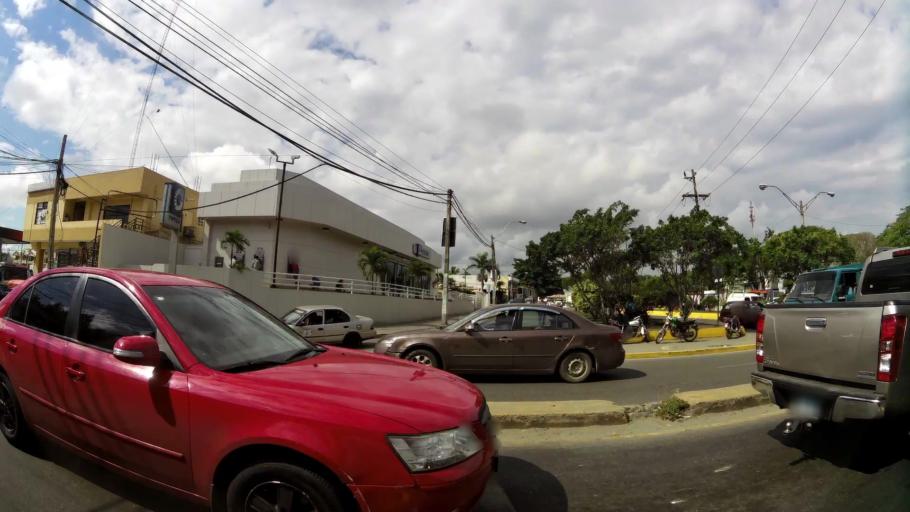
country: DO
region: Santiago
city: Santiago de los Caballeros
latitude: 19.4767
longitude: -70.7238
